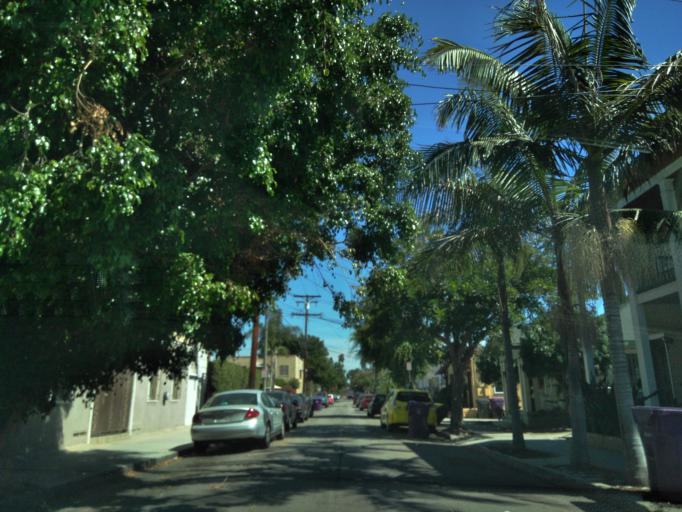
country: US
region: California
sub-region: Los Angeles County
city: Long Beach
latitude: 33.7708
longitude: -118.1705
